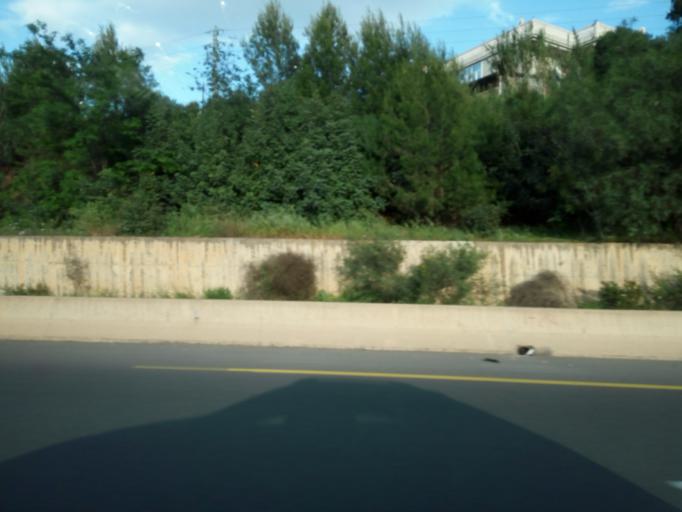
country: DZ
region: Tipaza
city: El Affroun
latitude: 36.4237
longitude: 2.5675
